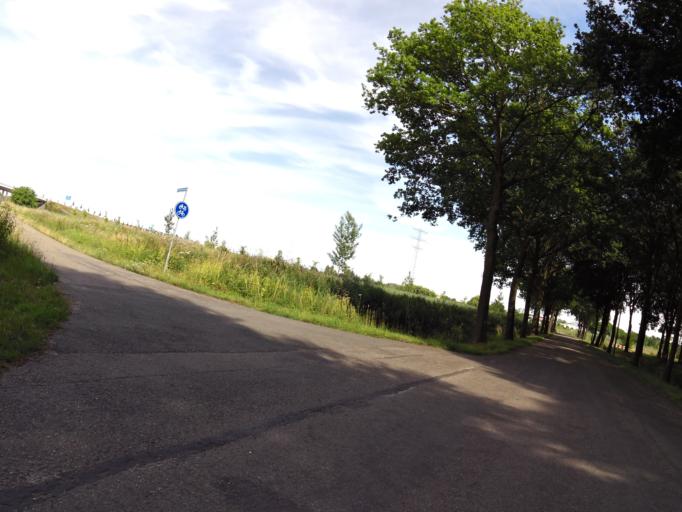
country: NL
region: North Brabant
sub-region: Gemeente 's-Hertogenbosch
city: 's-Hertogenbosch
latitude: 51.7259
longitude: 5.3375
